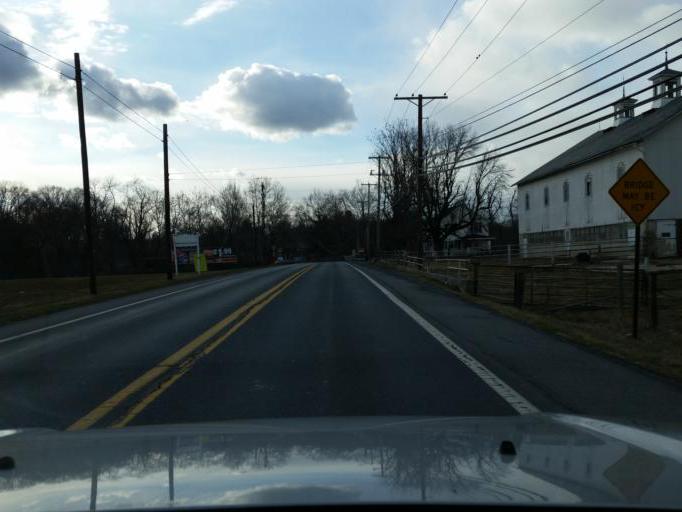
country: US
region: Pennsylvania
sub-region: Dauphin County
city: Middletown
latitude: 40.1992
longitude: -76.7141
